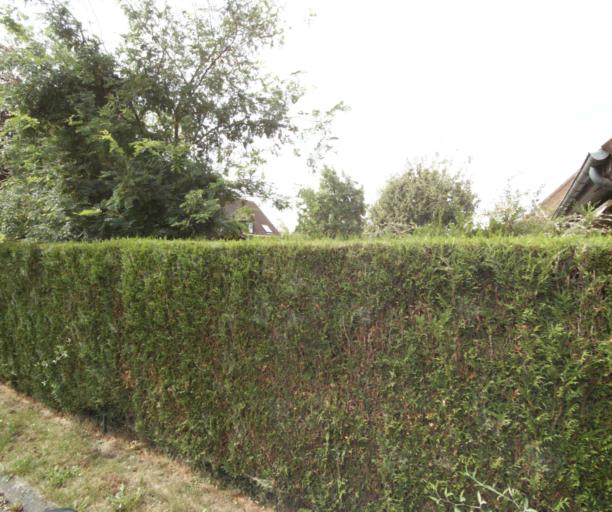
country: FR
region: Nord-Pas-de-Calais
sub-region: Departement du Nord
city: Saint-Andre-lez-Lille
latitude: 50.6659
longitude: 3.0378
